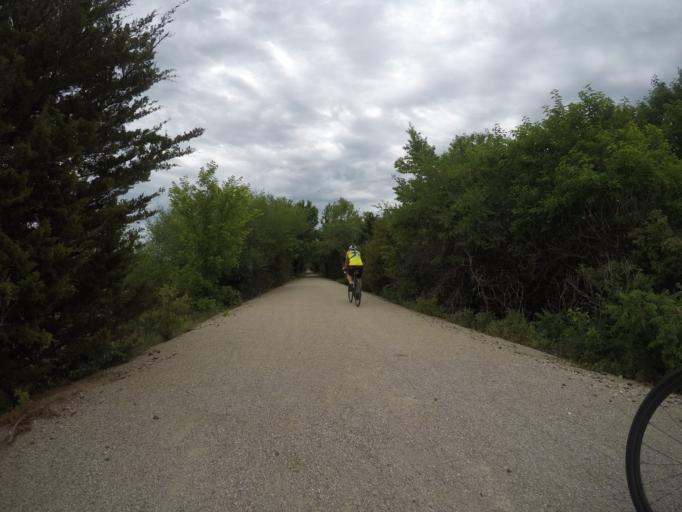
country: US
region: Kansas
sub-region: Anderson County
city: Garnett
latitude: 38.2951
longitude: -95.2433
